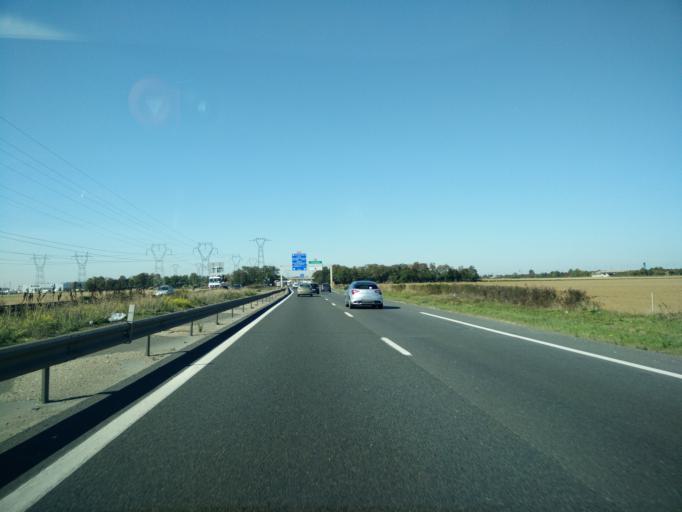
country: FR
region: Ile-de-France
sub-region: Departement de Seine-et-Marne
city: Mitry-Mory
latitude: 48.9709
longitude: 2.5962
